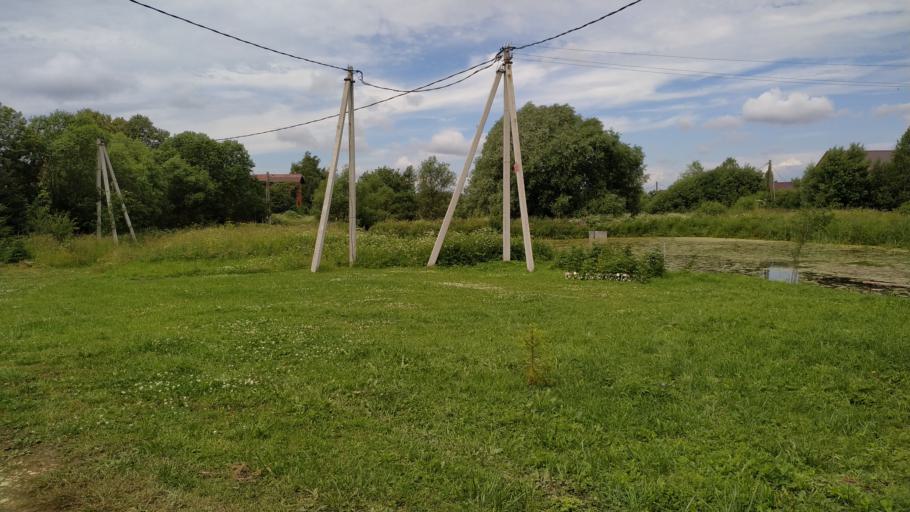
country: RU
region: Moskovskaya
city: Dorokhovo
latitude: 55.5561
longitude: 36.3178
